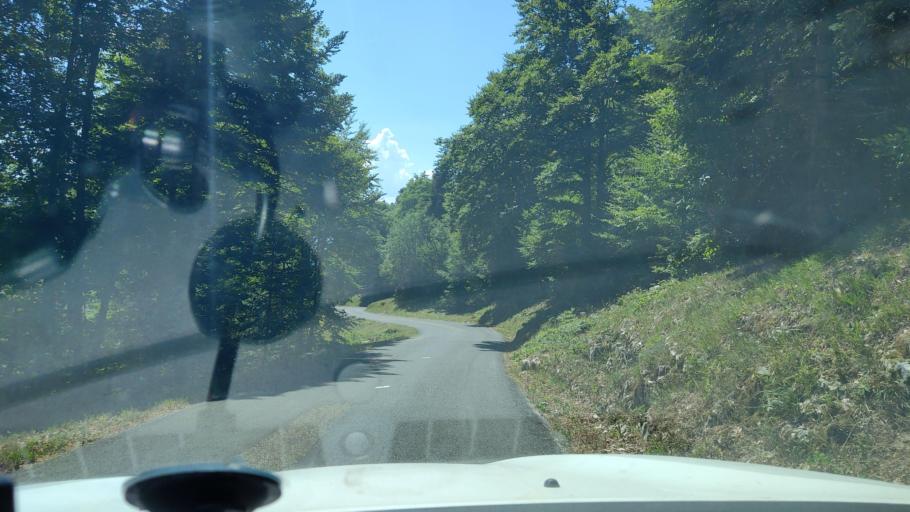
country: FR
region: Rhone-Alpes
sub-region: Departement de la Savoie
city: Le Bourget-du-Lac
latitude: 45.6611
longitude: 5.8244
